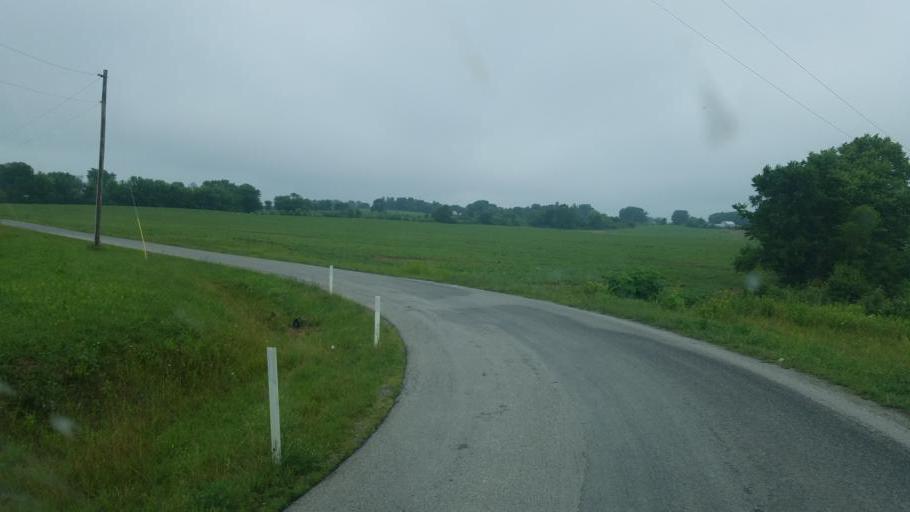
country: US
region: Ohio
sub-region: Highland County
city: Hillsboro
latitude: 39.2493
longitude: -83.5470
